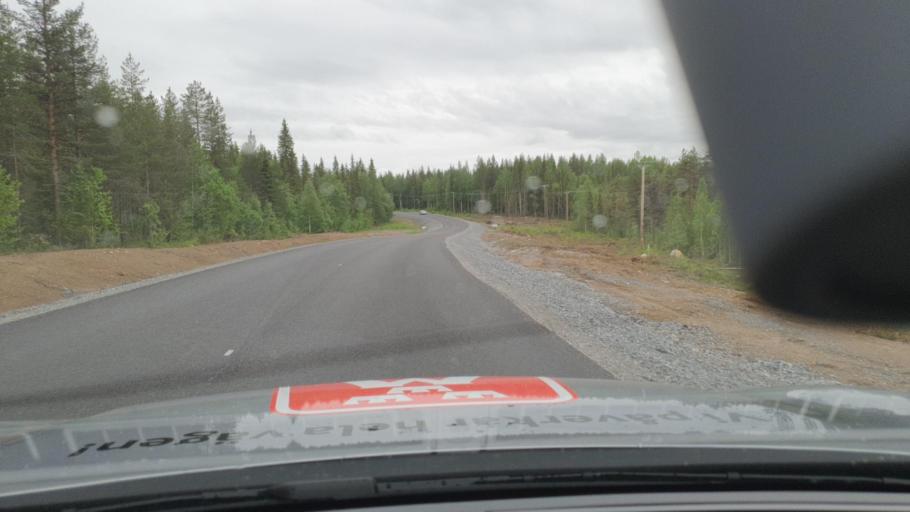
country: SE
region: Norrbotten
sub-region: Overkalix Kommun
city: OEverkalix
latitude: 66.6681
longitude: 23.2206
